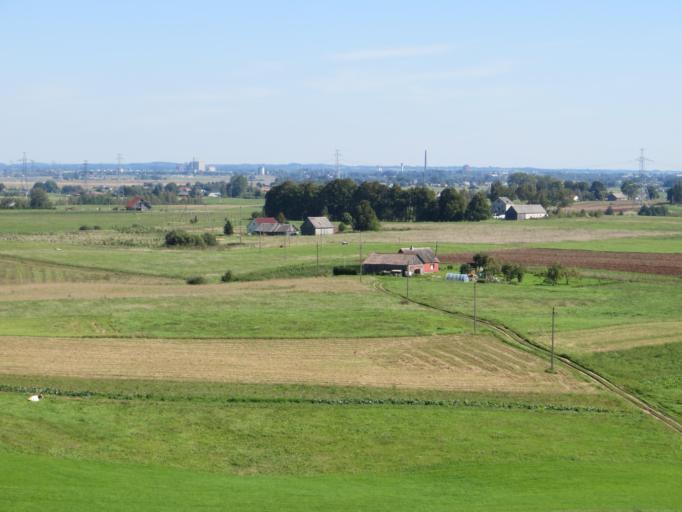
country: LT
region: Alytaus apskritis
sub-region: Alytus
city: Alytus
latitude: 54.4377
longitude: 23.8837
